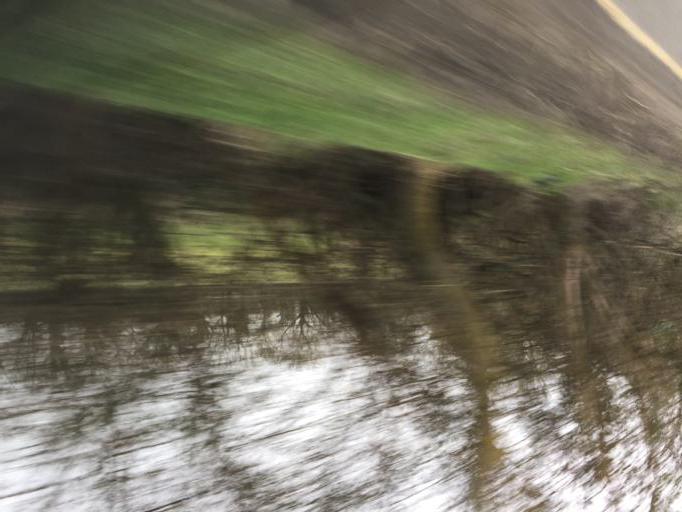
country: GB
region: England
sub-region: Oxfordshire
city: Wantage
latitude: 51.5942
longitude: -1.4587
